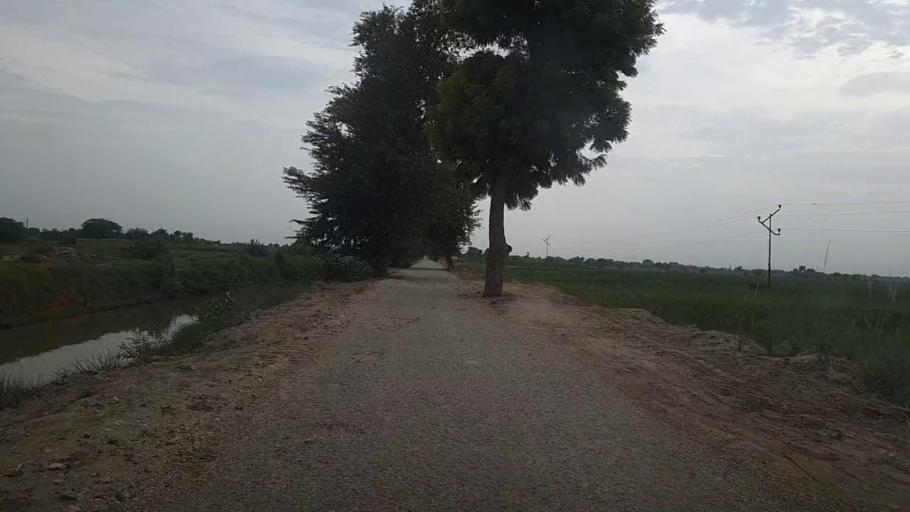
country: PK
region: Sindh
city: Karaundi
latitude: 26.9581
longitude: 68.3640
